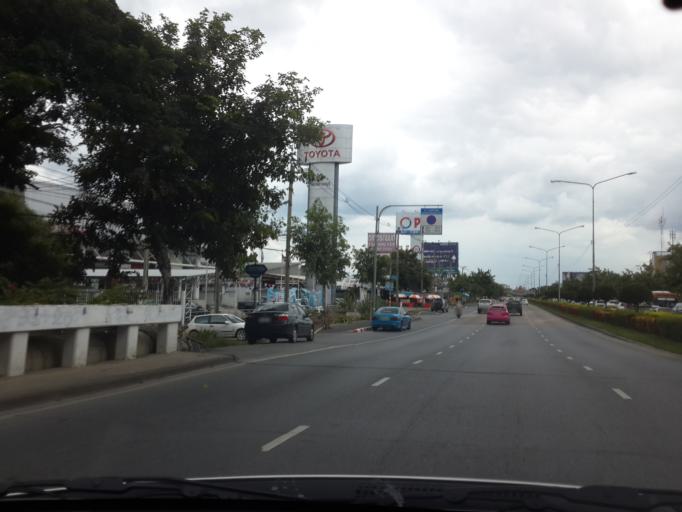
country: TH
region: Bangkok
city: Saphan Sung
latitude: 13.7902
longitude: 100.6975
